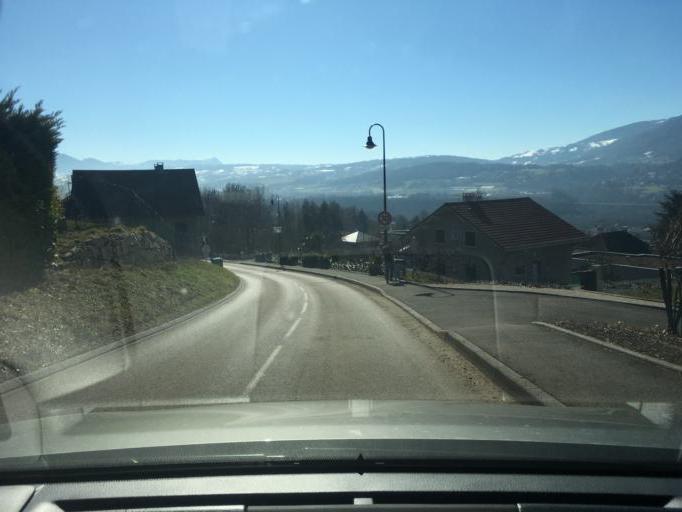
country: FR
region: Rhone-Alpes
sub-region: Departement de la Haute-Savoie
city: Vetraz-Monthoux
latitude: 46.1801
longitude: 6.2582
